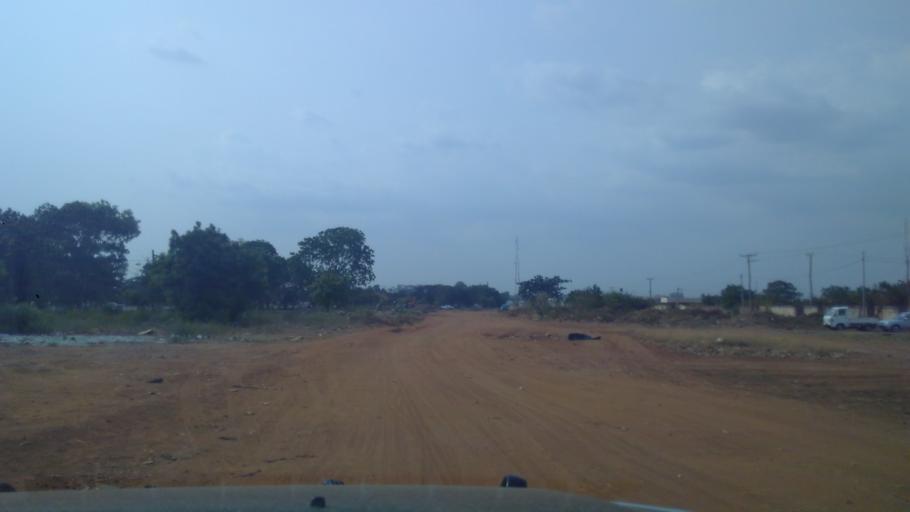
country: GH
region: Greater Accra
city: Tema
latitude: 5.6761
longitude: -0.0101
